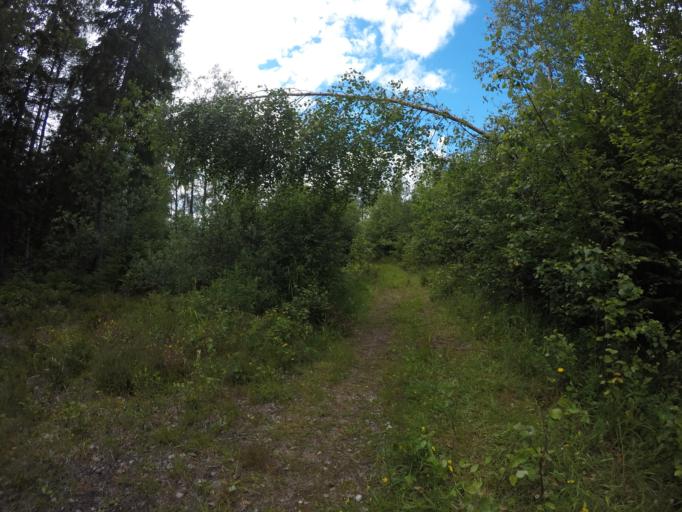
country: SE
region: OErebro
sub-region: Hallefors Kommun
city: Haellefors
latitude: 60.0446
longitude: 14.5085
